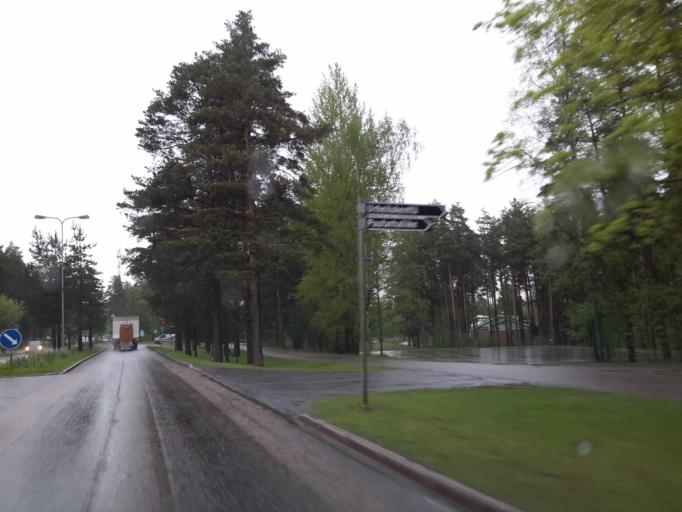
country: FI
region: Uusimaa
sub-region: Helsinki
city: Vihti
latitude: 60.3404
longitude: 24.3214
